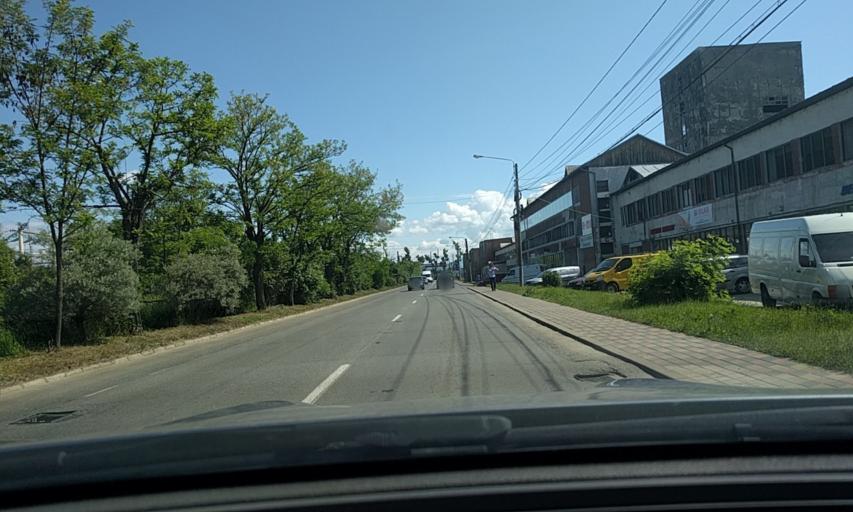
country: RO
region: Bistrita-Nasaud
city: Bistrita
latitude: 47.1360
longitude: 24.4773
